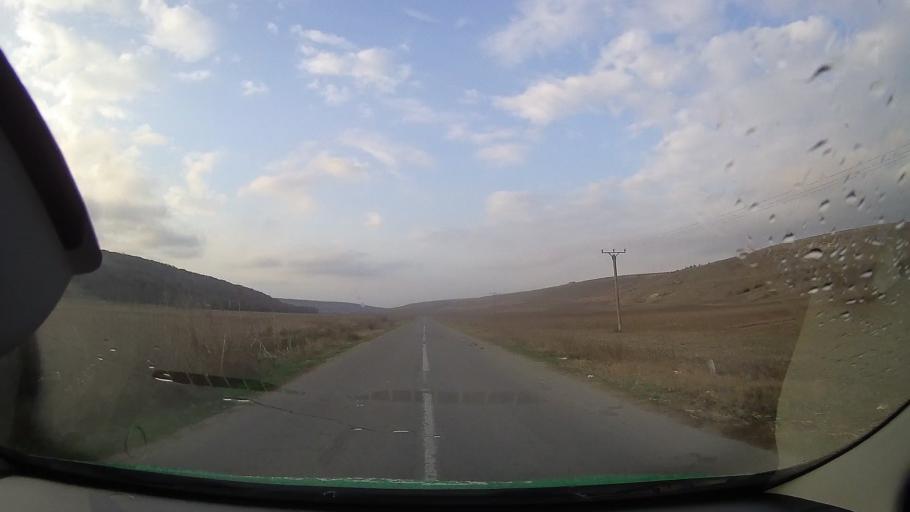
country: RO
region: Constanta
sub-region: Comuna Dobromir
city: Dobromir
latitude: 44.0230
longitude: 27.8695
